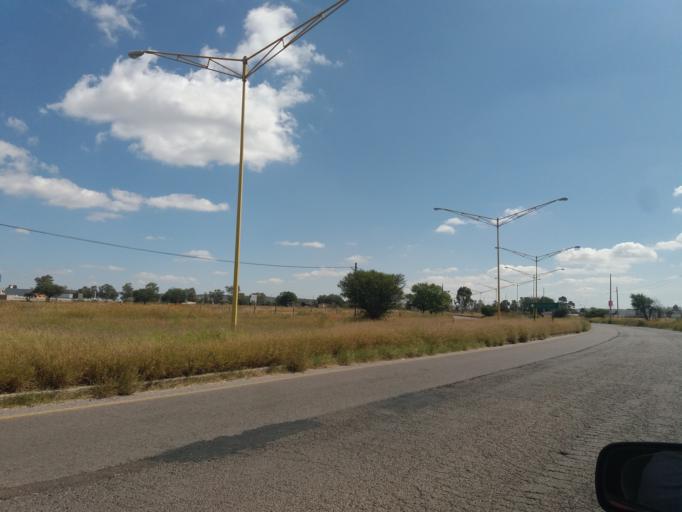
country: MX
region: Aguascalientes
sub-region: Aguascalientes
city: San Sebastian [Fraccionamiento]
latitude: 21.8199
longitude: -102.2919
